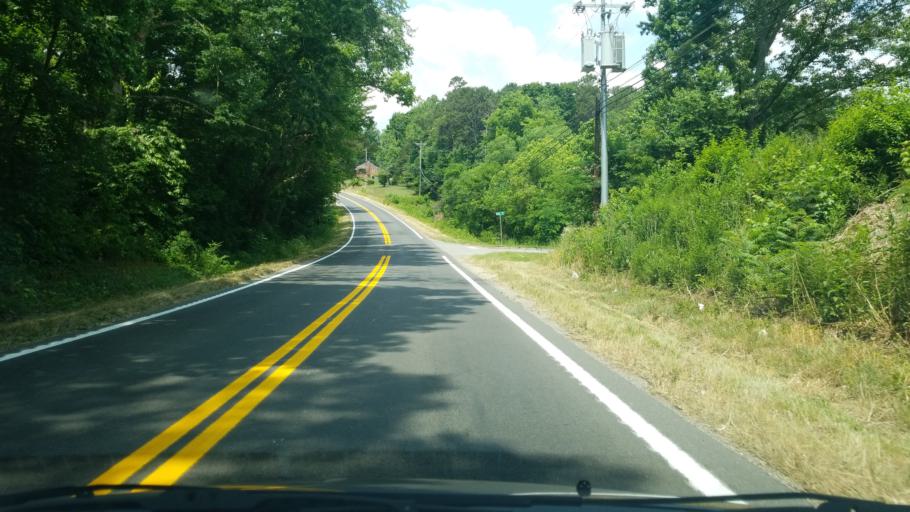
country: US
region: Tennessee
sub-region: Hamilton County
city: Lakesite
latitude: 35.2048
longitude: -85.1420
